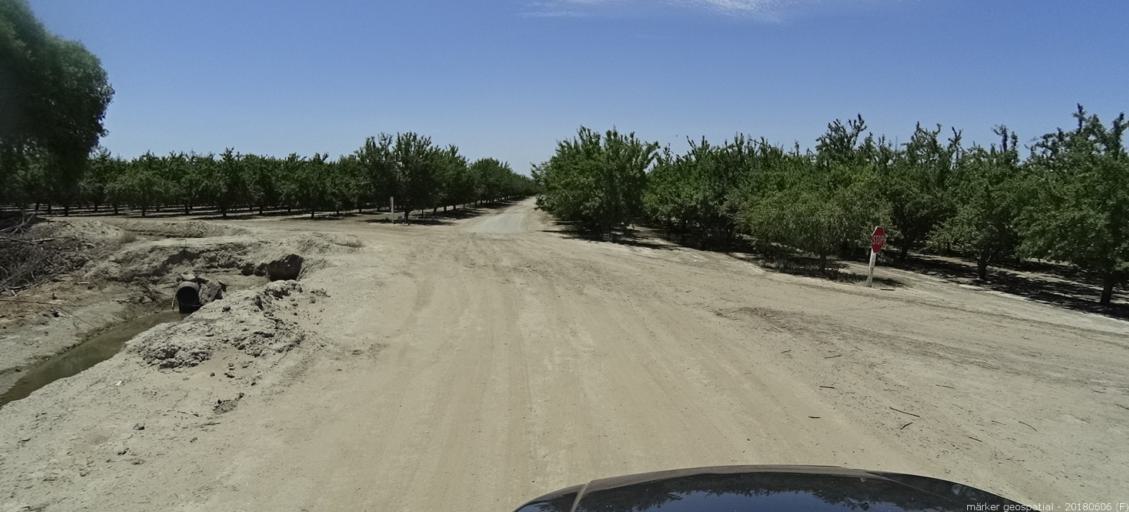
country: US
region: California
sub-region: Fresno County
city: Firebaugh
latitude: 36.8801
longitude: -120.3998
